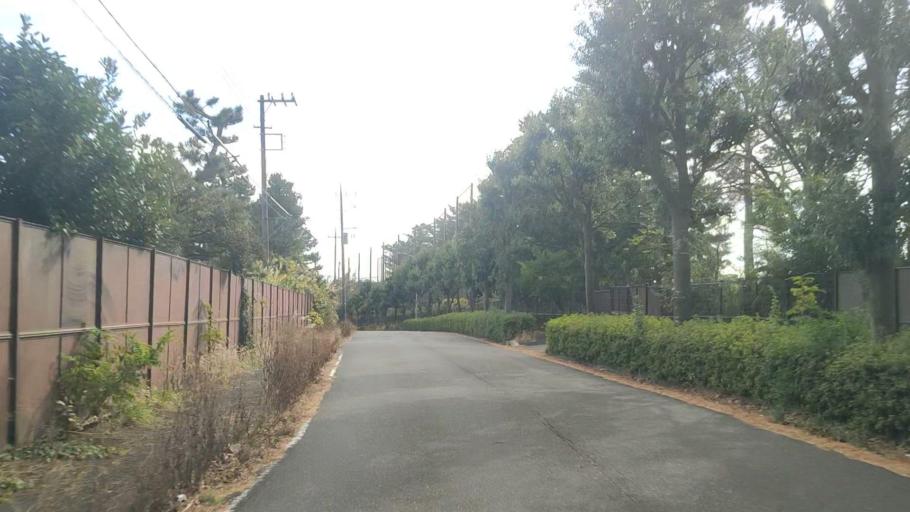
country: JP
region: Kanagawa
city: Yokohama
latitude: 35.4490
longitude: 139.5452
